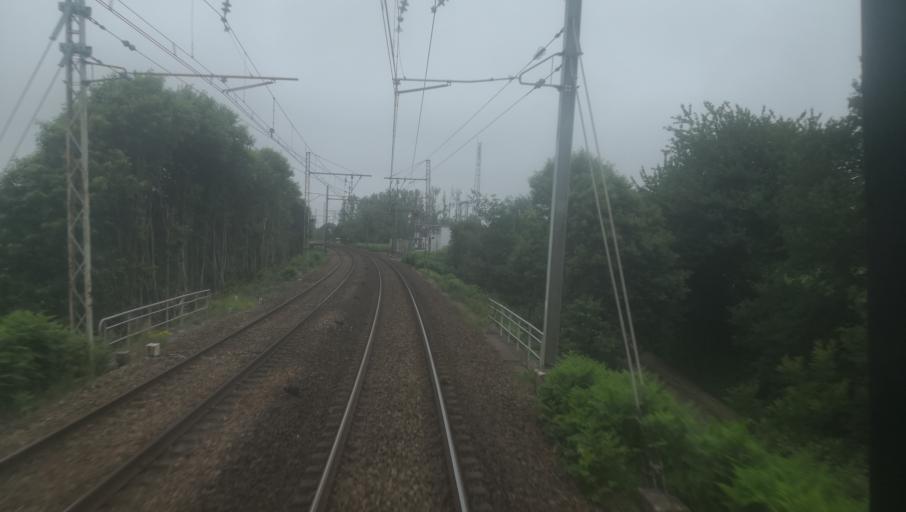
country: FR
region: Limousin
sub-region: Departement de la Creuse
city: Saint-Agnant-de-Versillat
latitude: 46.3393
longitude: 1.5384
